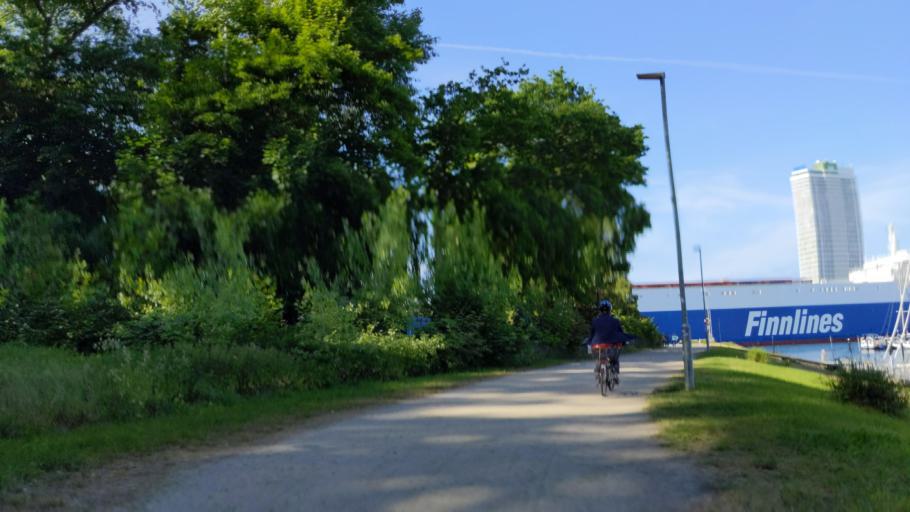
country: DE
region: Schleswig-Holstein
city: Travemuende
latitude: 53.9565
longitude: 10.8758
